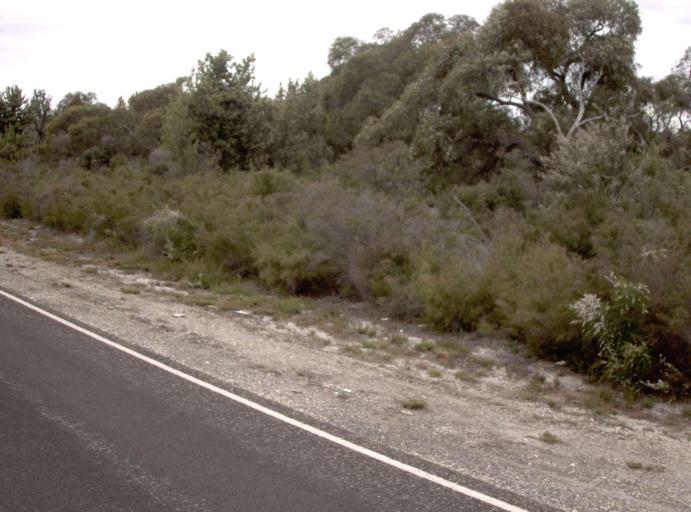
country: AU
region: Victoria
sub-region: Wellington
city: Sale
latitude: -38.1829
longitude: 147.3745
